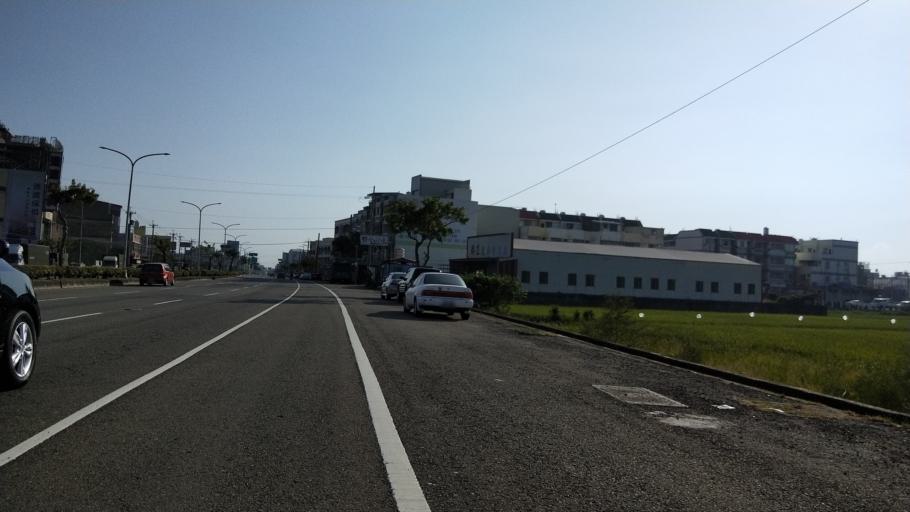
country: TW
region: Taiwan
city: Fengyuan
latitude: 24.2601
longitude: 120.5600
